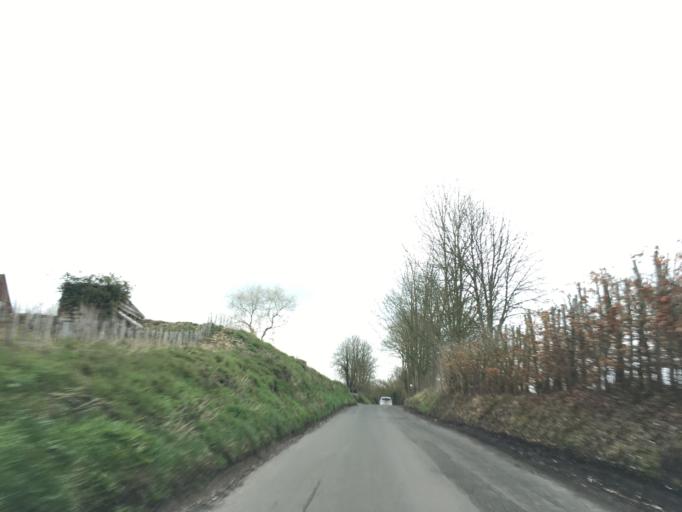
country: GB
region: England
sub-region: West Berkshire
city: Hungerford
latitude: 51.4281
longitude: -1.5215
